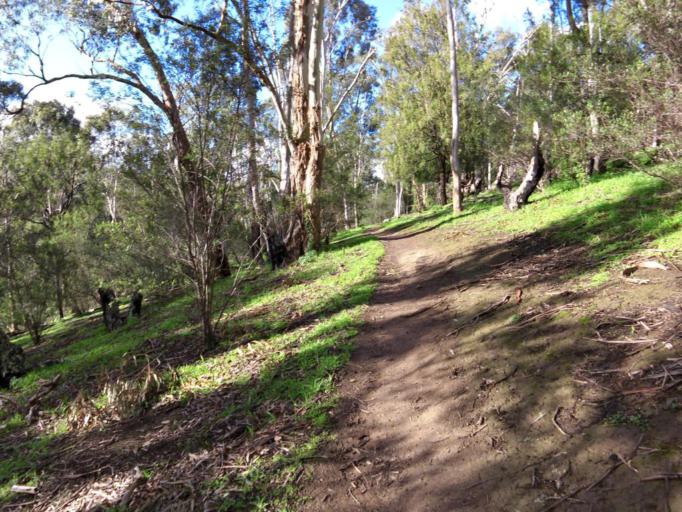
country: AU
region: Victoria
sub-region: Banyule
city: Watsonia North
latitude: -37.6818
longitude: 145.0839
